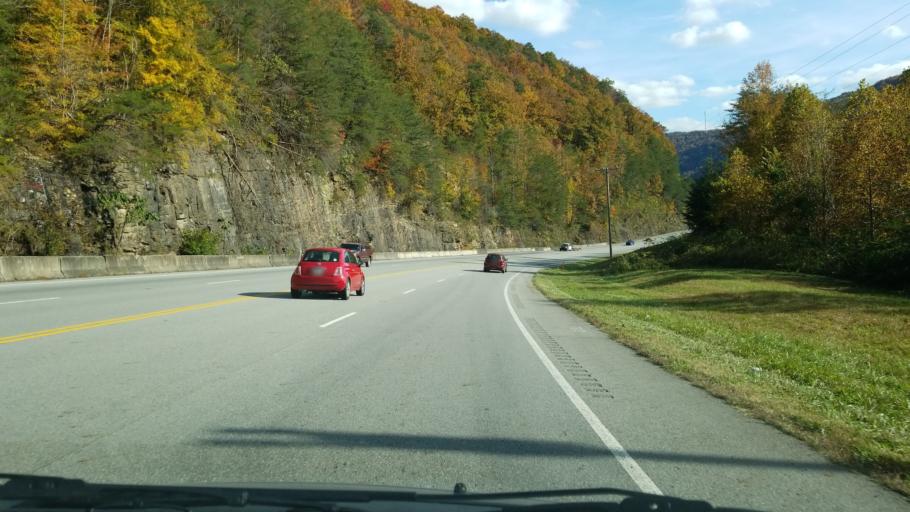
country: US
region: Tennessee
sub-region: Sequatchie County
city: Dunlap
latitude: 35.4166
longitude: -85.4144
